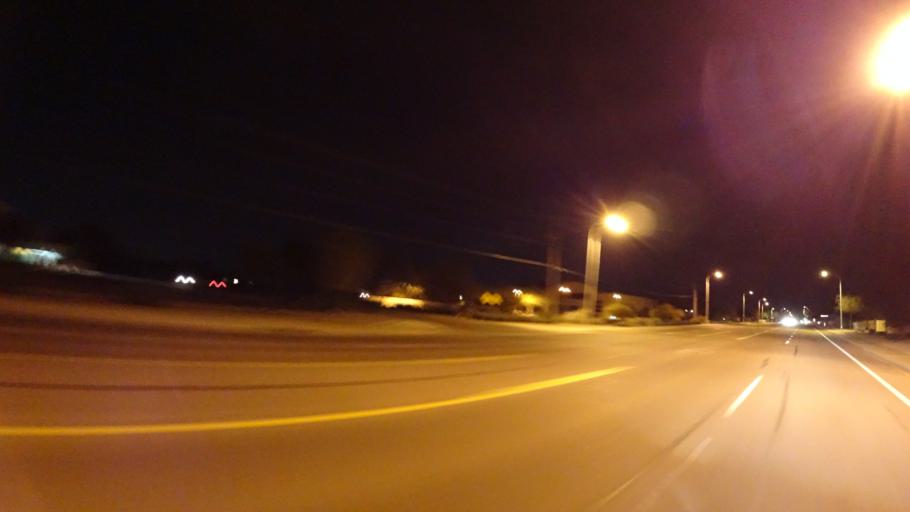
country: US
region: Arizona
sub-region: Maricopa County
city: San Carlos
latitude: 33.3349
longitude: -111.8866
